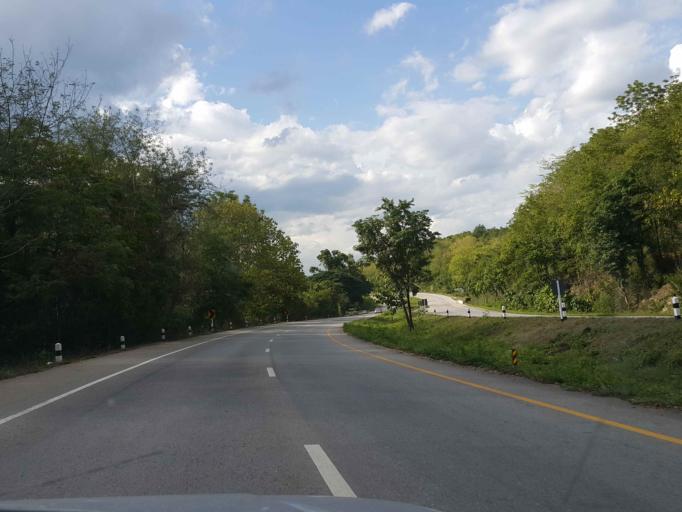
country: TH
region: Lampang
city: Thoen
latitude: 17.6925
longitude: 99.2325
